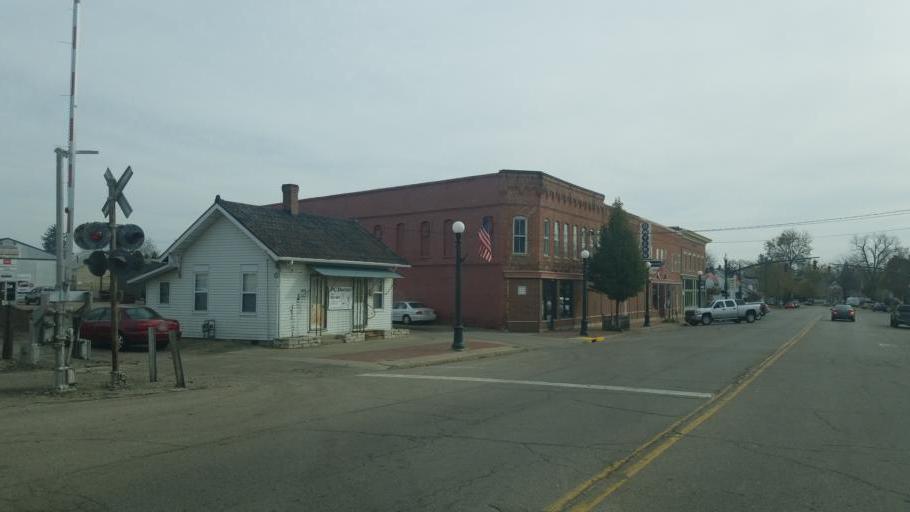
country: US
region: Ohio
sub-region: Madison County
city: London
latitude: 39.8836
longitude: -83.4455
